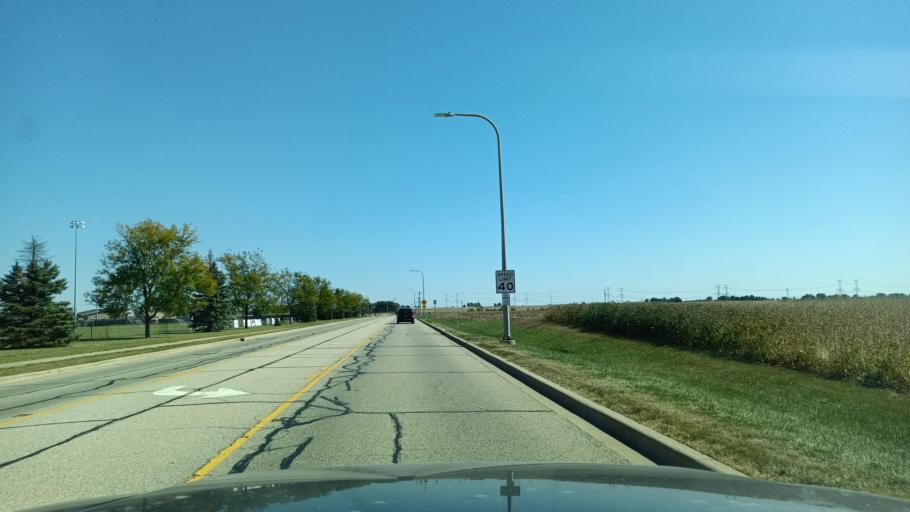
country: US
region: Illinois
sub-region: Tazewell County
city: Morton
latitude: 40.6133
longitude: -89.4357
